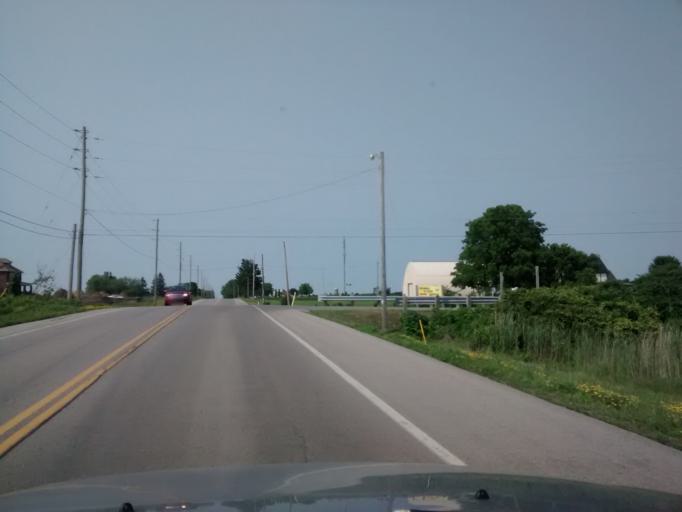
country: CA
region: Ontario
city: Ancaster
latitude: 43.0706
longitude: -79.9260
